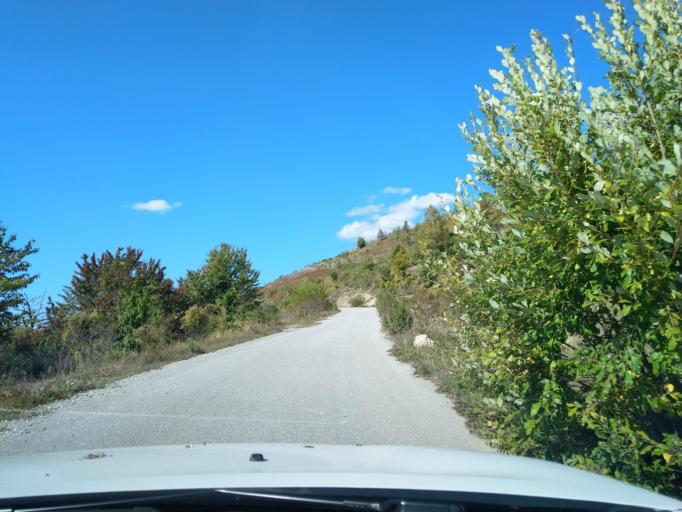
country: RS
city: Sokolovica
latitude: 43.2488
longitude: 20.3273
